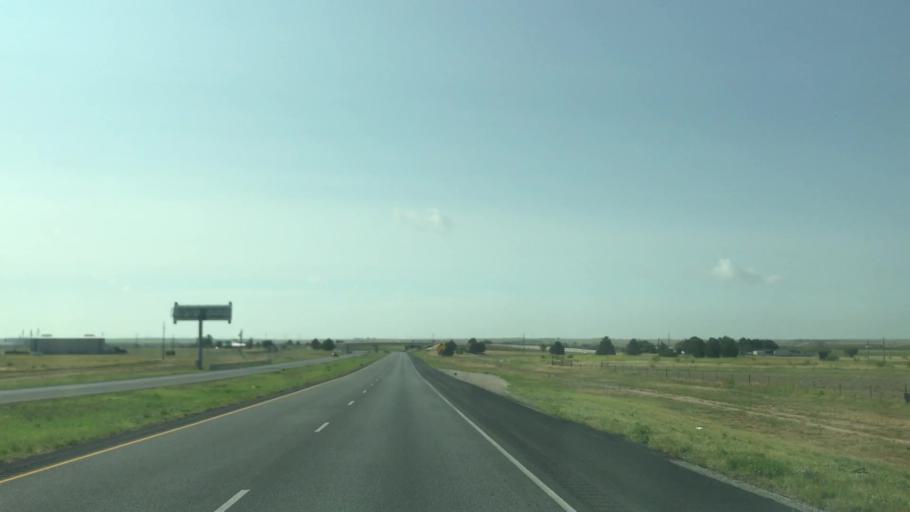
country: US
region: Texas
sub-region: Scurry County
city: Snyder
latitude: 32.6961
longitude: -100.8625
